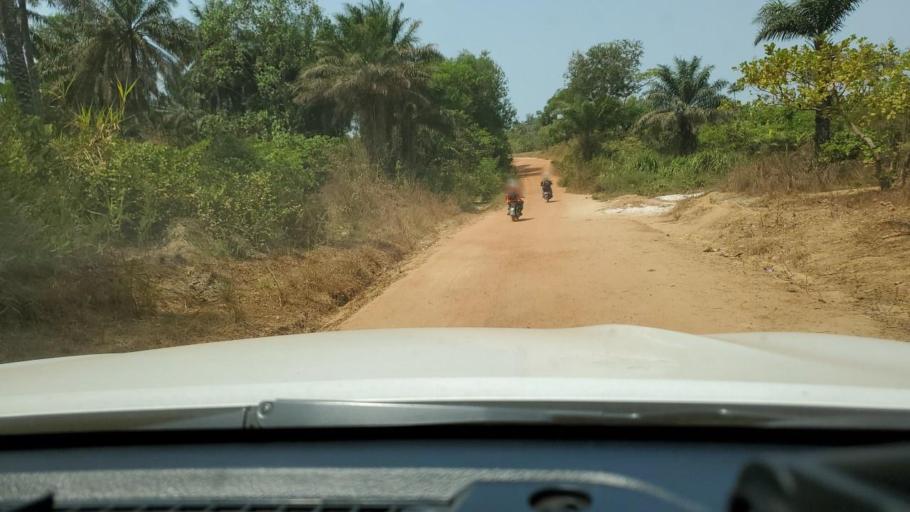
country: GN
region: Boke
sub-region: Boffa
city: Boffa
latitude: 10.0804
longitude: -13.8656
